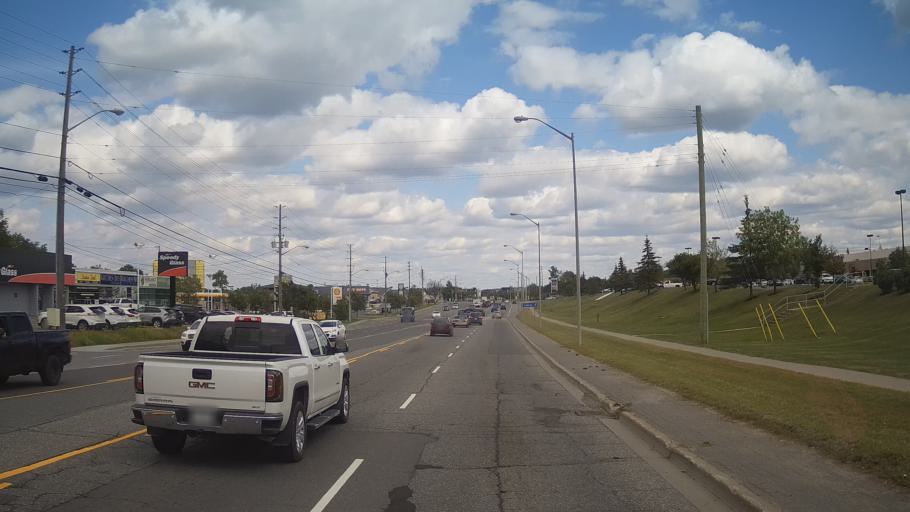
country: CA
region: Ontario
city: Greater Sudbury
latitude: 46.5040
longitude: -80.9494
